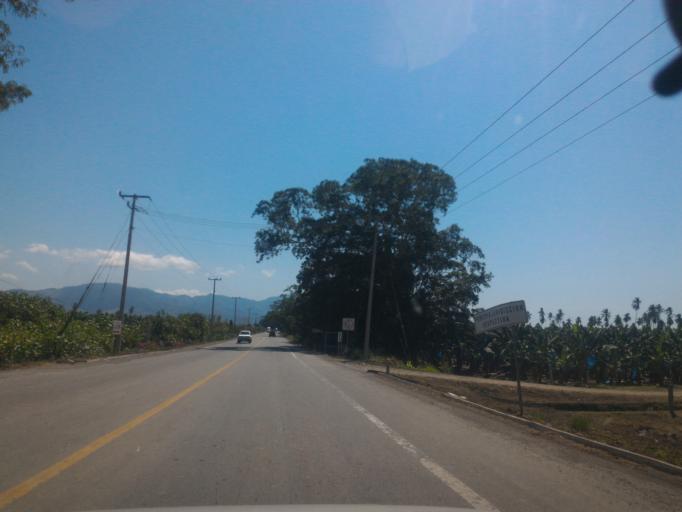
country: MX
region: Michoacan
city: Coahuayana Viejo
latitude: 18.7142
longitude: -103.7136
